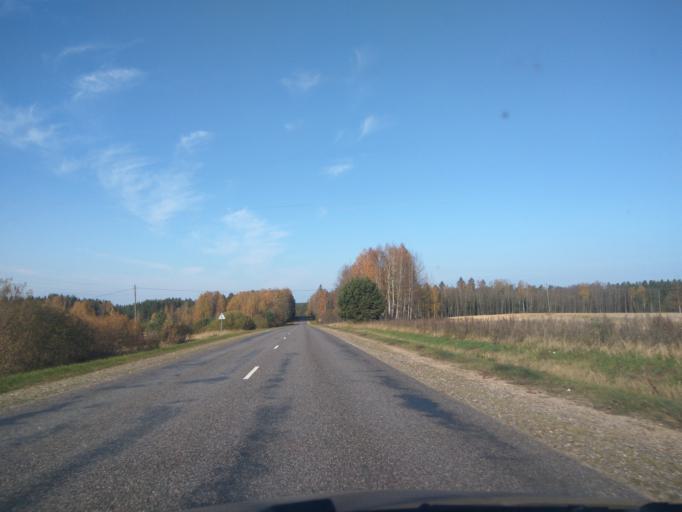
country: LV
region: Kuldigas Rajons
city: Kuldiga
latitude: 57.0555
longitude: 21.8172
